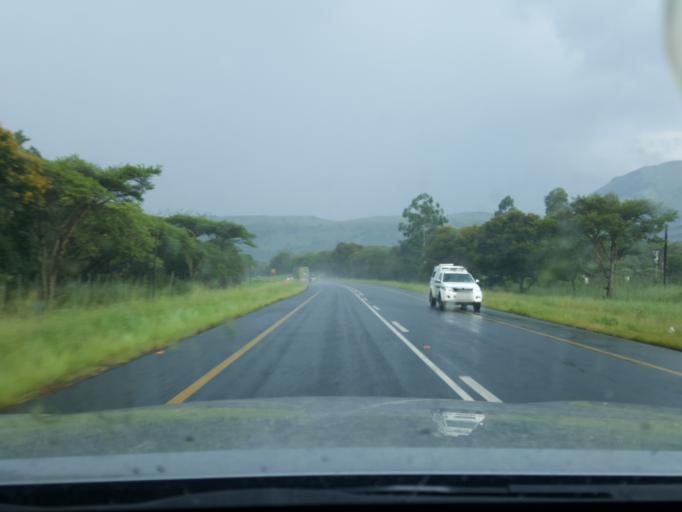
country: ZA
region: Mpumalanga
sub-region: Nkangala District Municipality
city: Belfast
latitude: -25.6114
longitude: 30.4252
